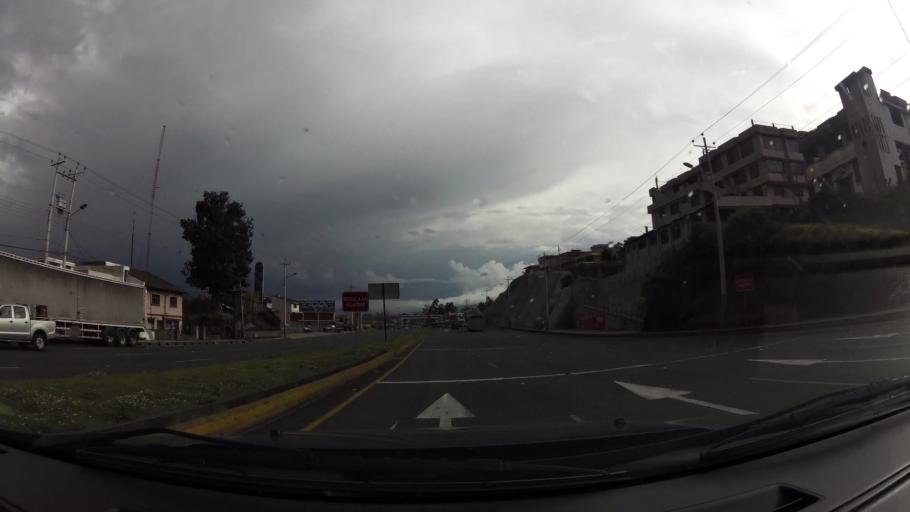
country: EC
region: Pichincha
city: Machachi
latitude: -0.4028
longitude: -78.5456
